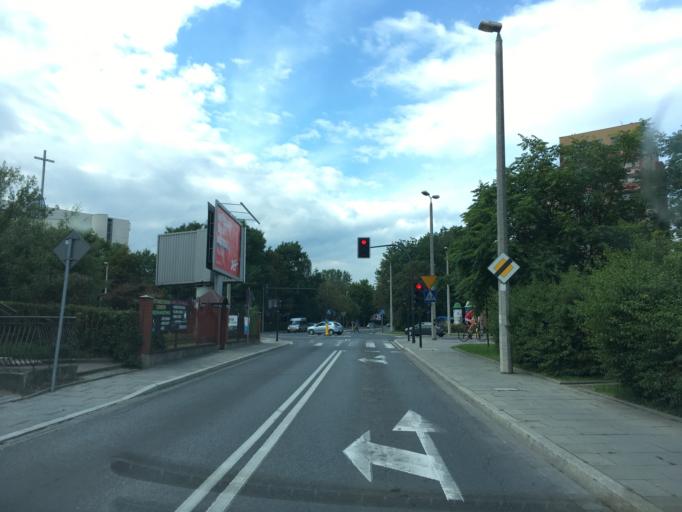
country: PL
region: Lesser Poland Voivodeship
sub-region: Krakow
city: Krakow
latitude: 50.0834
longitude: 19.9249
